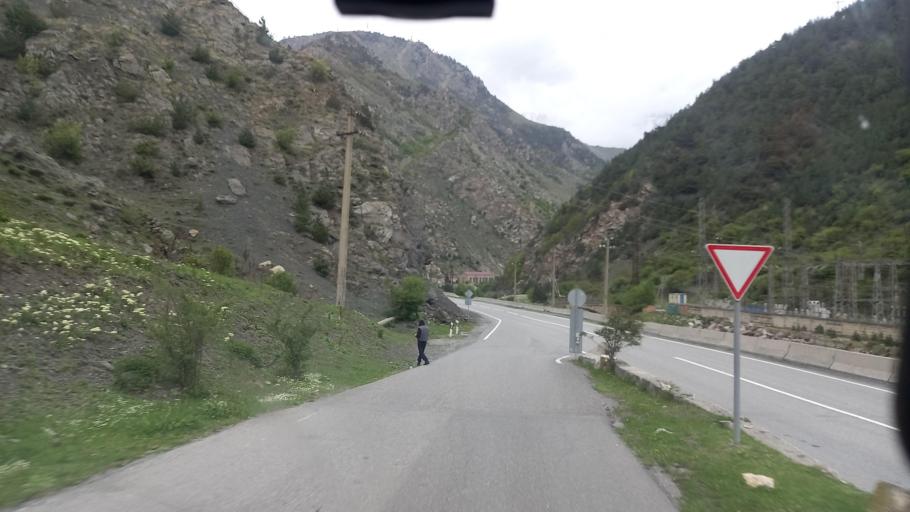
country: RU
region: North Ossetia
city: Mizur
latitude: 42.8338
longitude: 44.0265
